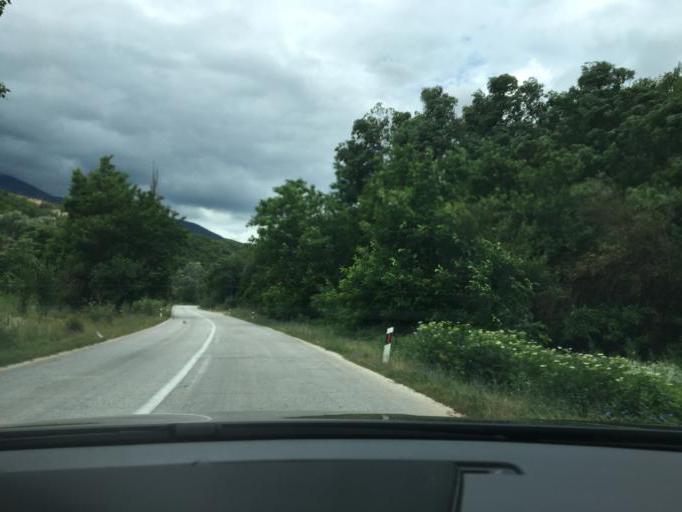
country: MK
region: Kriva Palanka
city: Kriva Palanka
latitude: 42.1760
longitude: 22.2376
